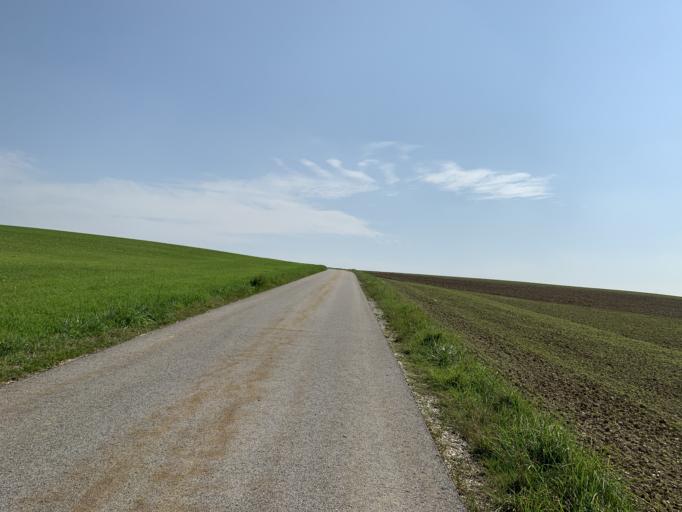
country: DE
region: Bavaria
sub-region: Upper Bavaria
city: Marzling
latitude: 48.4149
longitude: 11.8196
